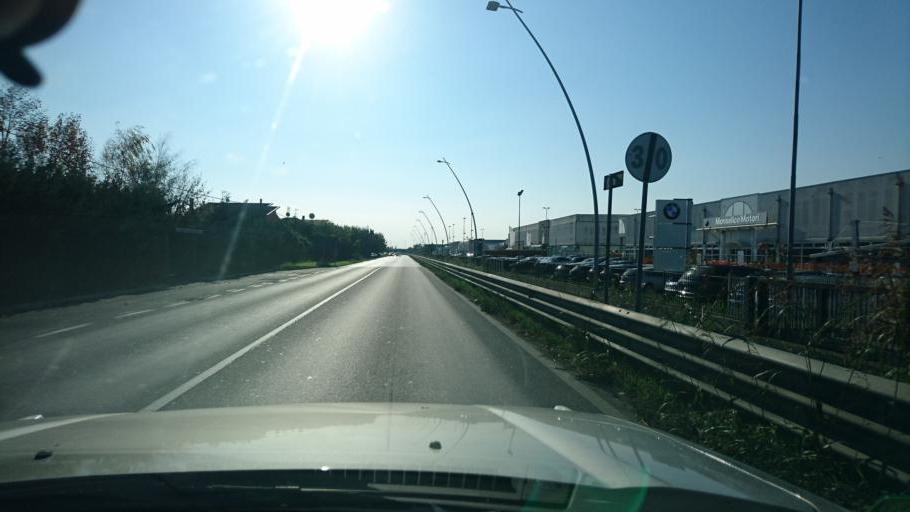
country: IT
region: Veneto
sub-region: Provincia di Padova
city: Monselice
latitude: 45.2166
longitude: 11.7552
